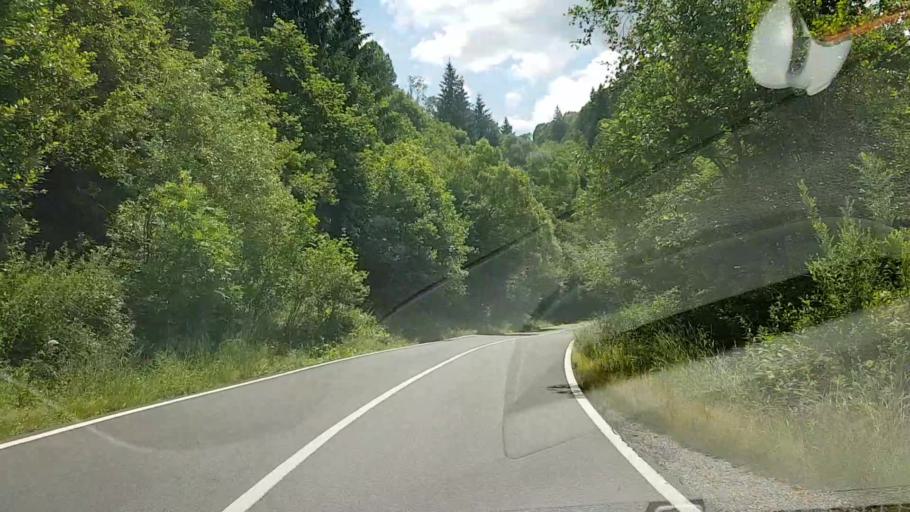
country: RO
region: Suceava
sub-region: Comuna Crucea
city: Crucea
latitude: 47.3891
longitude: 25.5811
